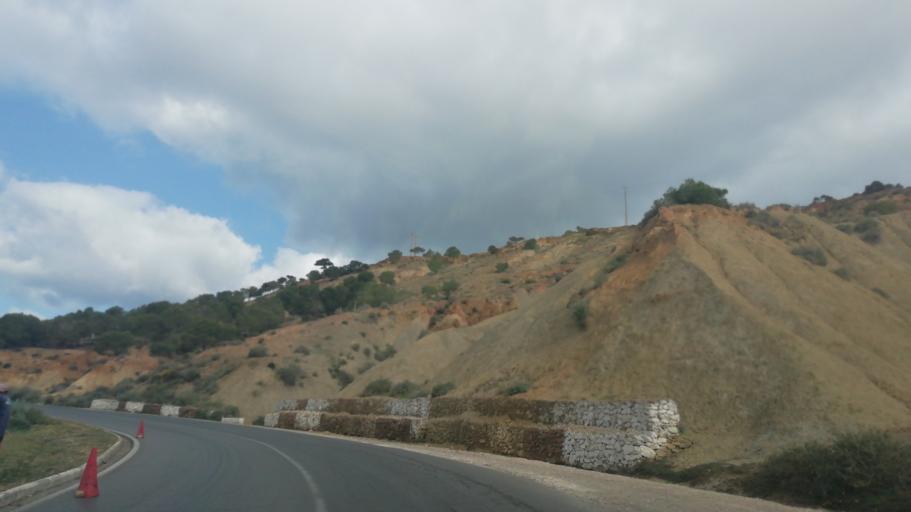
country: DZ
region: Relizane
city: Mazouna
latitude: 36.3070
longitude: 0.6712
